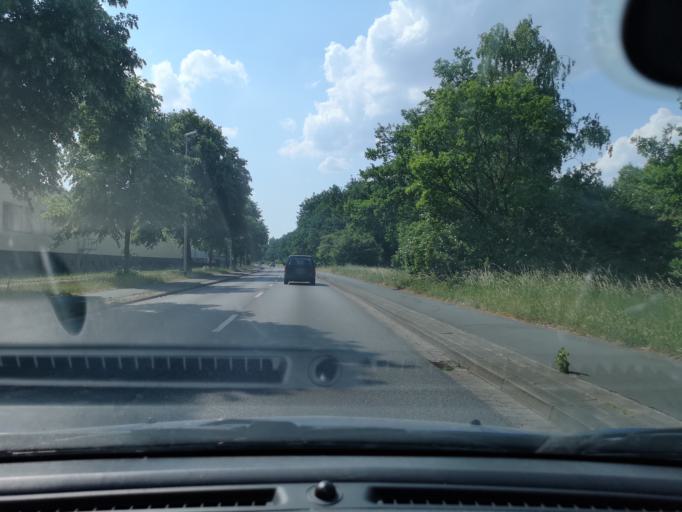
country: DE
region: Lower Saxony
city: Langenhagen
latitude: 52.4212
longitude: 9.7505
